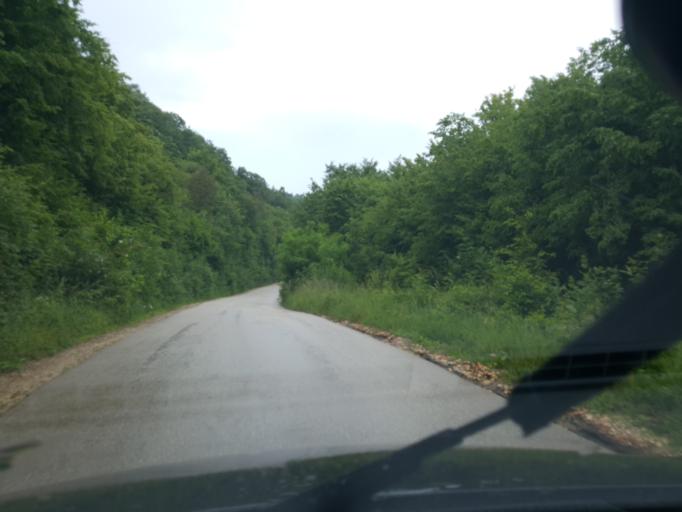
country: RS
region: Central Serbia
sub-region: Zajecarski Okrug
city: Boljevac
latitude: 43.7945
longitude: 21.9065
